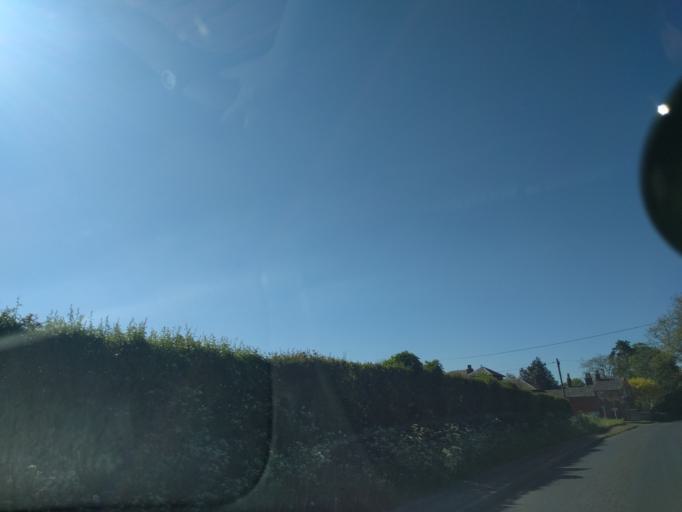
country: GB
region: England
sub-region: Wiltshire
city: Bratton
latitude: 51.3059
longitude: -2.1331
